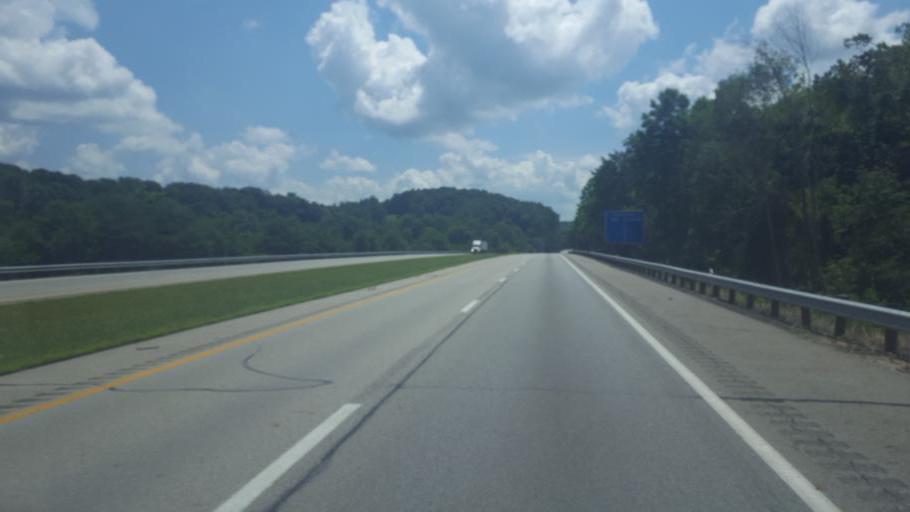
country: US
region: Ohio
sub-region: Jackson County
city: Jackson
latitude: 39.1077
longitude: -82.6760
